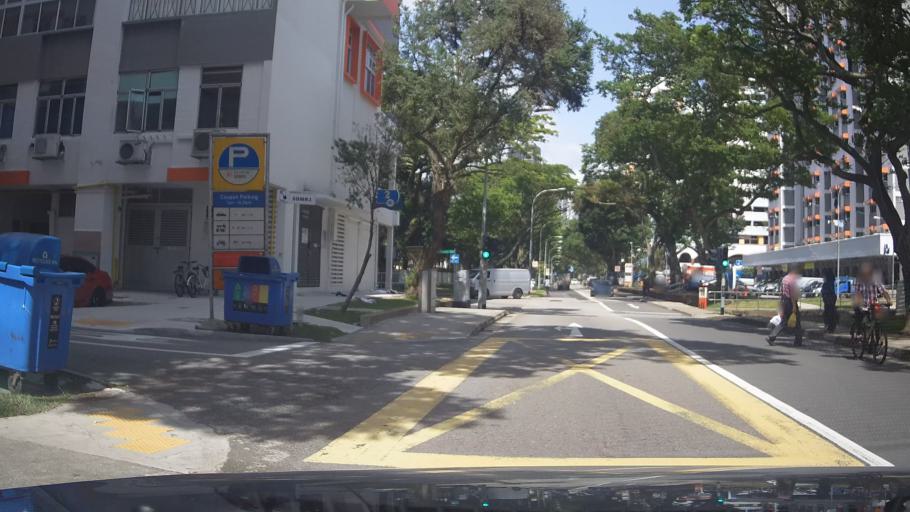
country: SG
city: Singapore
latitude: 1.3074
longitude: 103.8592
